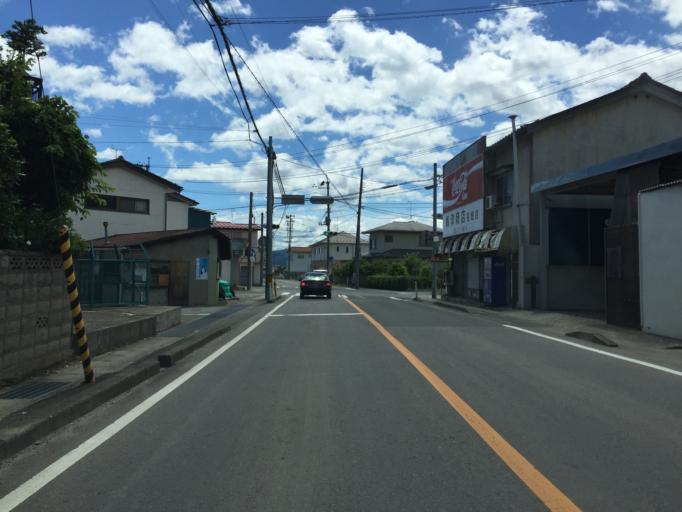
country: JP
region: Fukushima
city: Fukushima-shi
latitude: 37.7716
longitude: 140.4149
